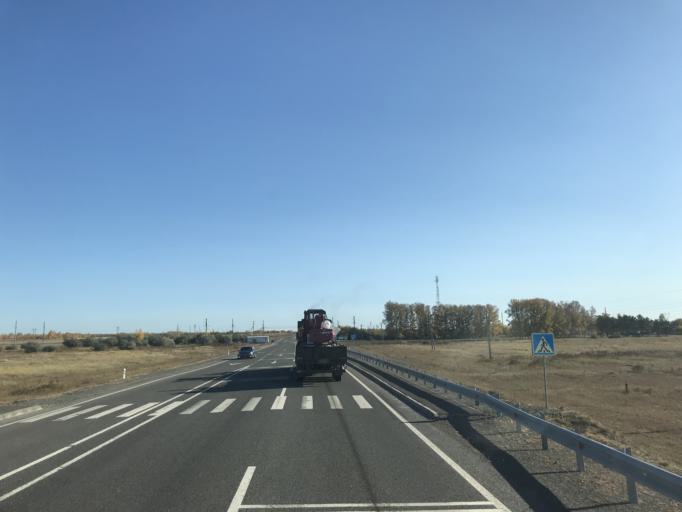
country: KZ
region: Pavlodar
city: Koktobe
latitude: 51.9283
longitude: 77.3317
